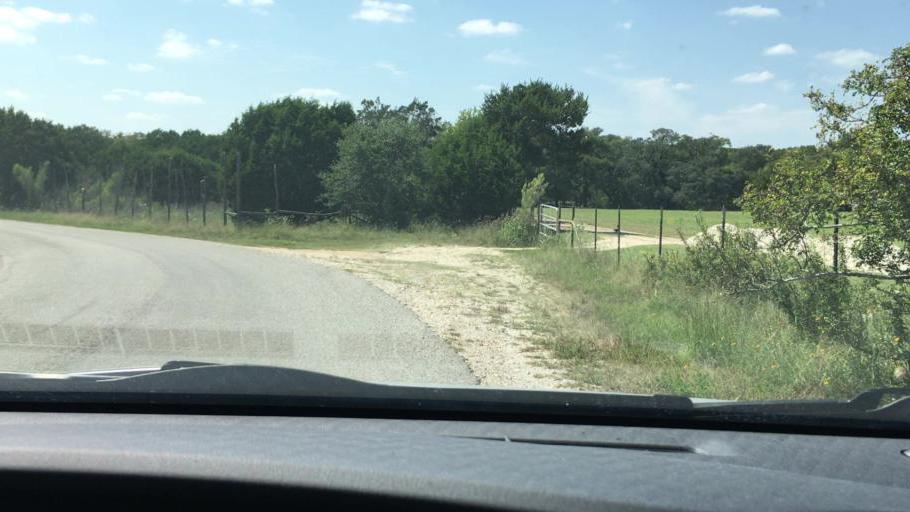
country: US
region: Texas
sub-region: Travis County
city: Shady Hollow
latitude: 30.1739
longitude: -97.9658
